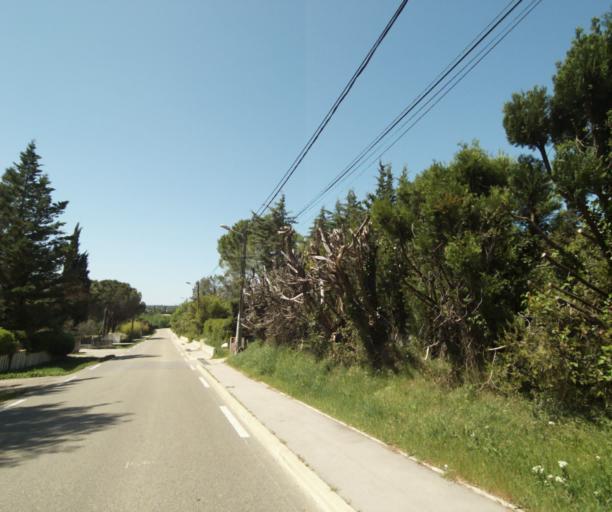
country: FR
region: Languedoc-Roussillon
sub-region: Departement de l'Herault
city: Prades-le-Lez
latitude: 43.6913
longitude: 3.8785
